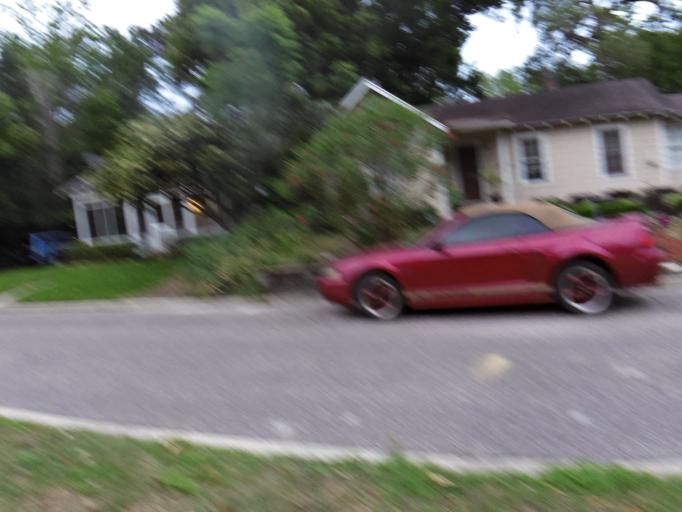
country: US
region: Florida
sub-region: Duval County
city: Jacksonville
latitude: 30.3046
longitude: -81.6500
